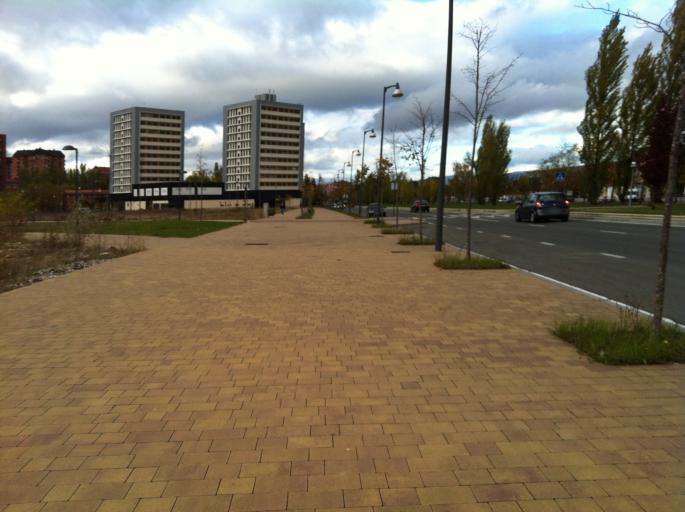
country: ES
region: Basque Country
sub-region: Provincia de Alava
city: Gasteiz / Vitoria
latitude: 42.8326
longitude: -2.6566
